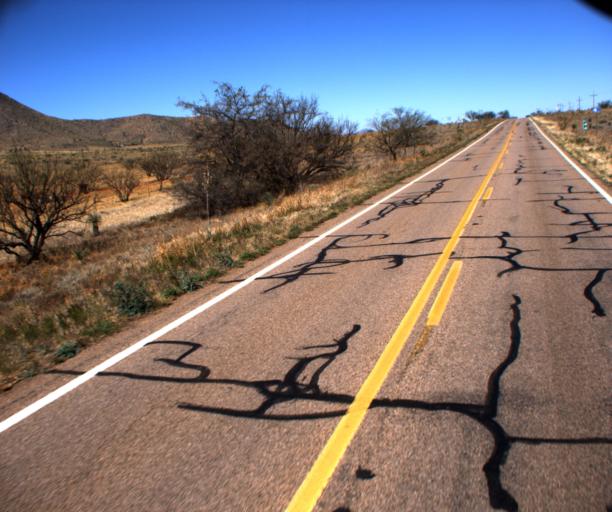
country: US
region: Arizona
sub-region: Cochise County
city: Huachuca City
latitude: 31.7174
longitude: -110.4710
